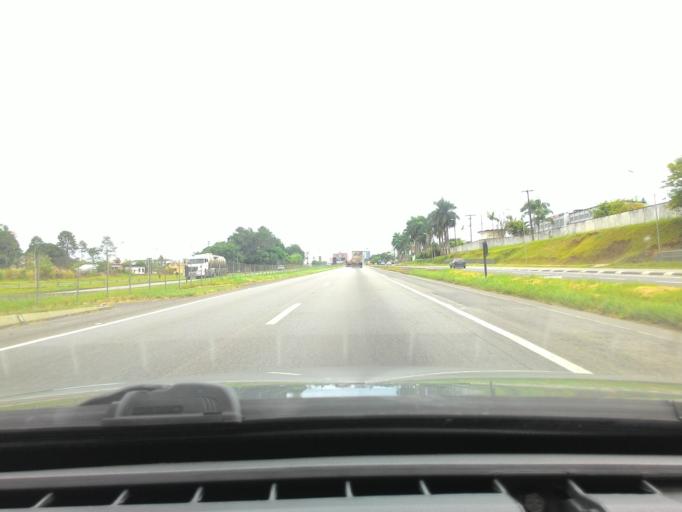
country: BR
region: Sao Paulo
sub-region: Registro
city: Registro
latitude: -24.5084
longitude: -47.8491
